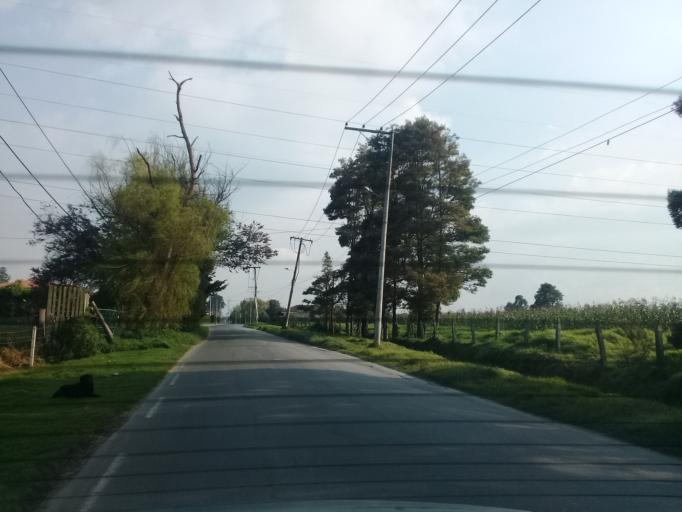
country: CO
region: Cundinamarca
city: Funza
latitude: 4.7371
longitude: -74.2236
